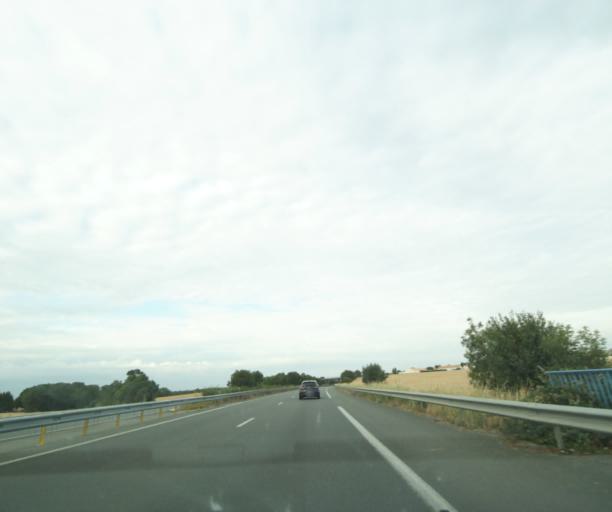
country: FR
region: Poitou-Charentes
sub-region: Departement de la Charente-Maritime
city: Dompierre-sur-Mer
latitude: 46.1933
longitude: -1.0655
